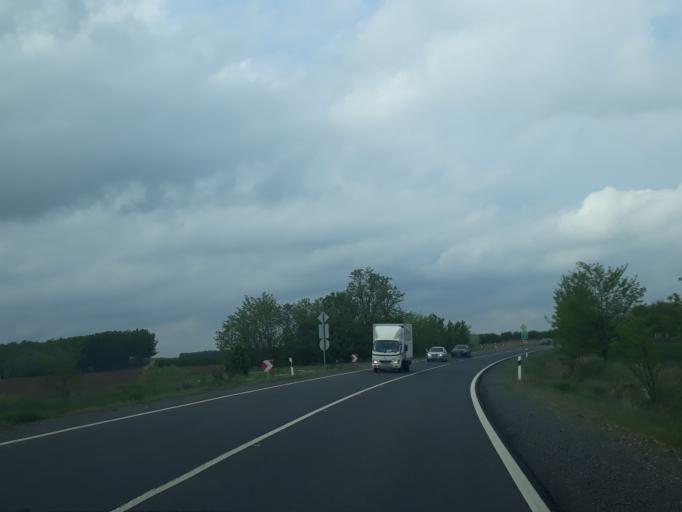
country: HU
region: Szabolcs-Szatmar-Bereg
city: Patroha
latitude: 48.1591
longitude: 22.0276
